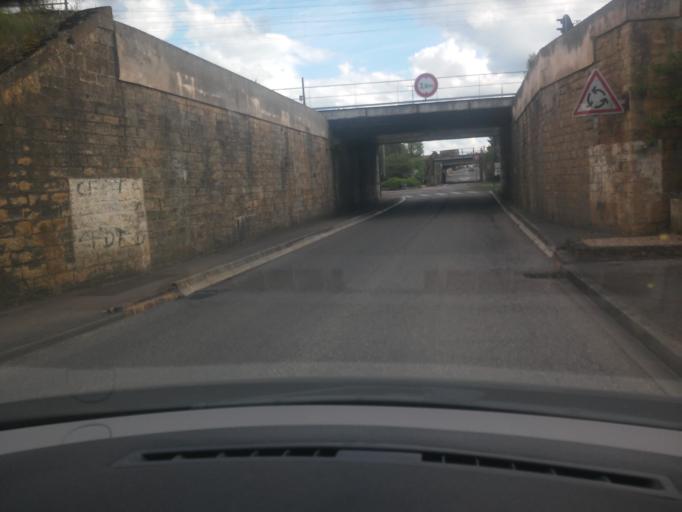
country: FR
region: Lorraine
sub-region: Departement de Meurthe-et-Moselle
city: Labry
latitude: 49.1669
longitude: 5.8818
